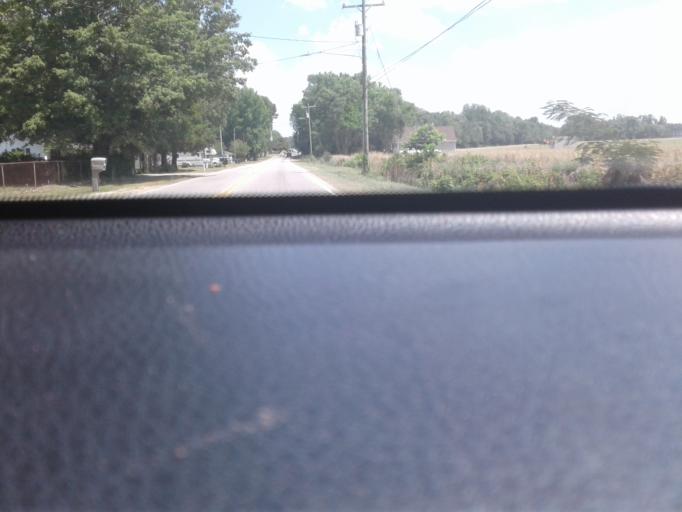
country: US
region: North Carolina
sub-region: Harnett County
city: Erwin
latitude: 35.3136
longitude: -78.6793
